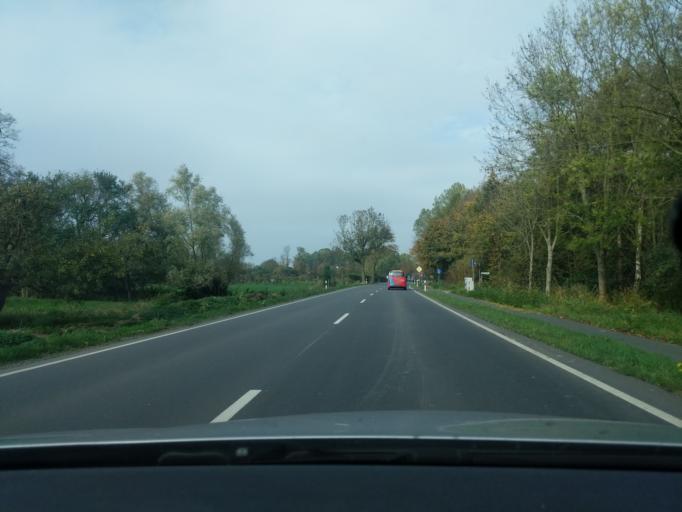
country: DE
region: Lower Saxony
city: Belum
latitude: 53.8132
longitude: 8.9956
